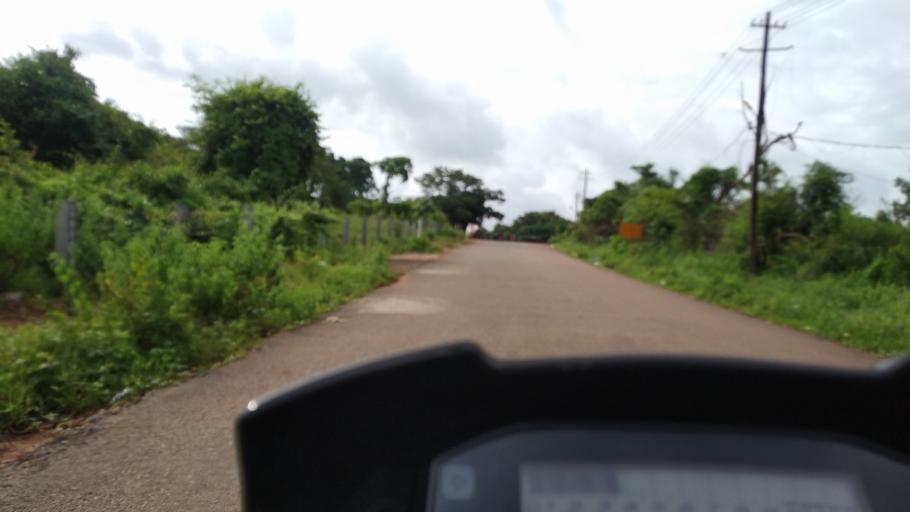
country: IN
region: Kerala
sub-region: Ernakulam
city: Aluva
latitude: 10.0509
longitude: 76.3451
